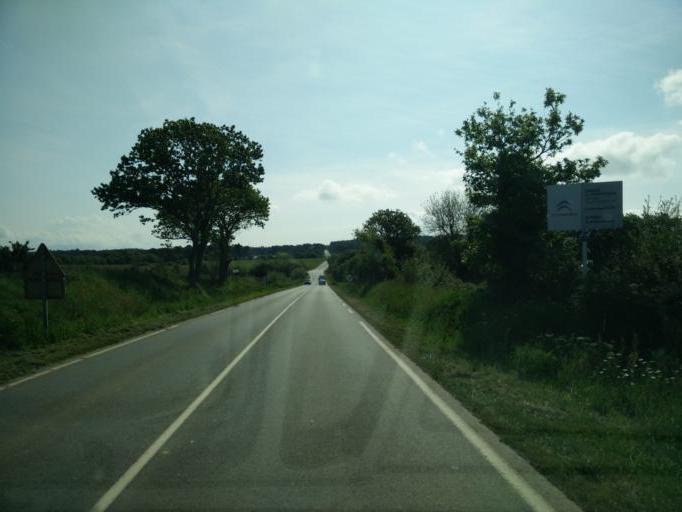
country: FR
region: Brittany
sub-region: Departement du Finistere
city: Crozon
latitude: 48.2487
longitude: -4.4583
